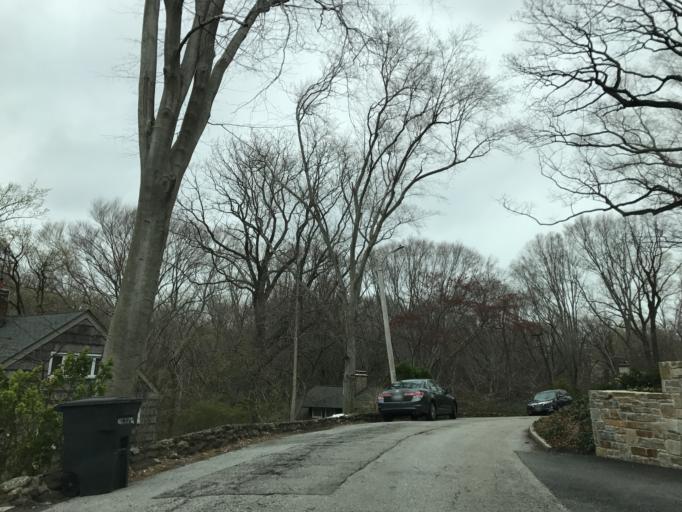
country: US
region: Maryland
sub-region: Baltimore County
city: Towson
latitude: 39.3570
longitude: -76.6410
